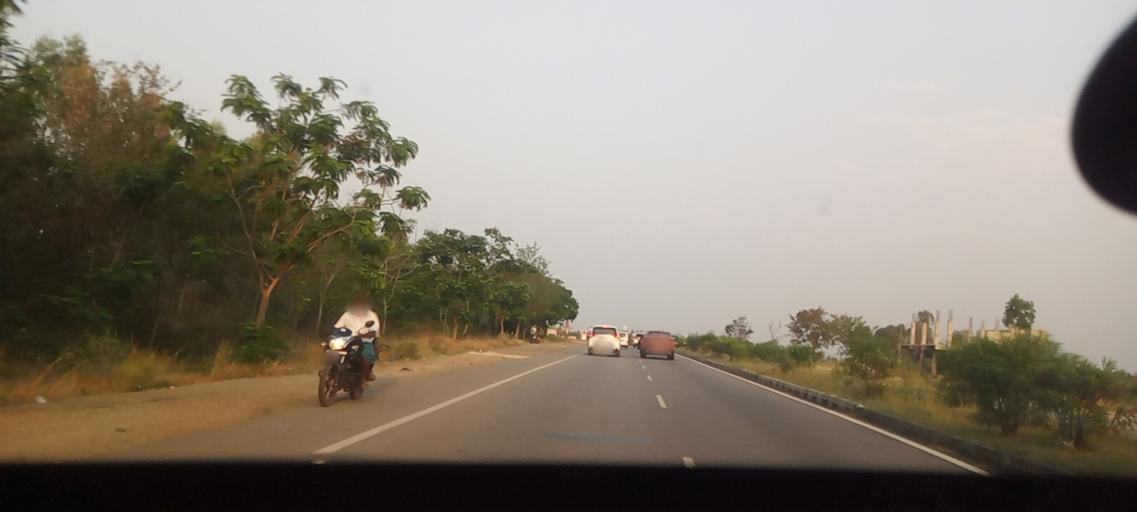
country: IN
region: Karnataka
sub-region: Tumkur
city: Kunigal
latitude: 12.9970
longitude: 76.9211
